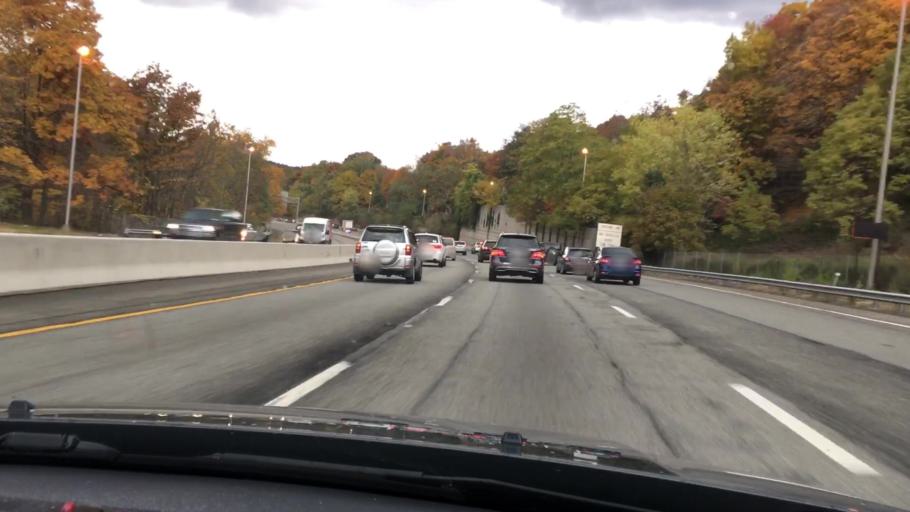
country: US
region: New Jersey
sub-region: Bergen County
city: Franklin Lakes
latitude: 41.0259
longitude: -74.2280
